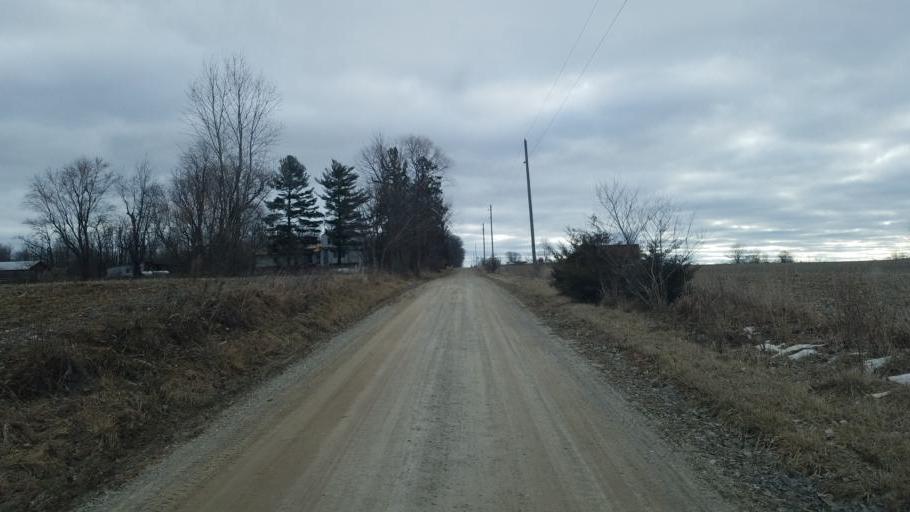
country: US
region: Ohio
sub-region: Richland County
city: Lexington
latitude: 40.5795
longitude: -82.6856
